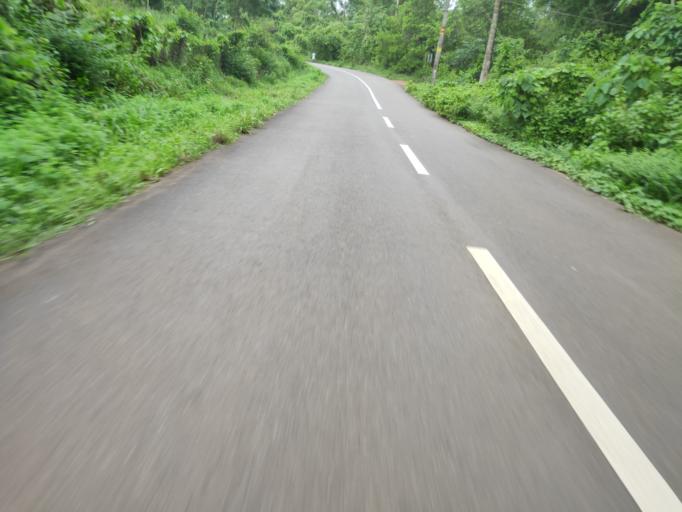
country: IN
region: Kerala
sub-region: Malappuram
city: Manjeri
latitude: 11.1707
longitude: 76.1812
